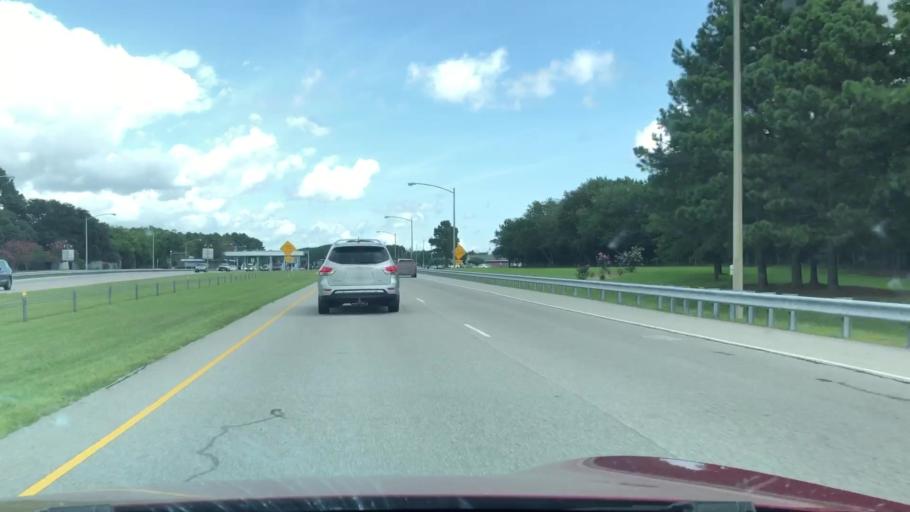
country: US
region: Virginia
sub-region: Northampton County
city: Cape Charles
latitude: 37.1298
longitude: -75.9671
